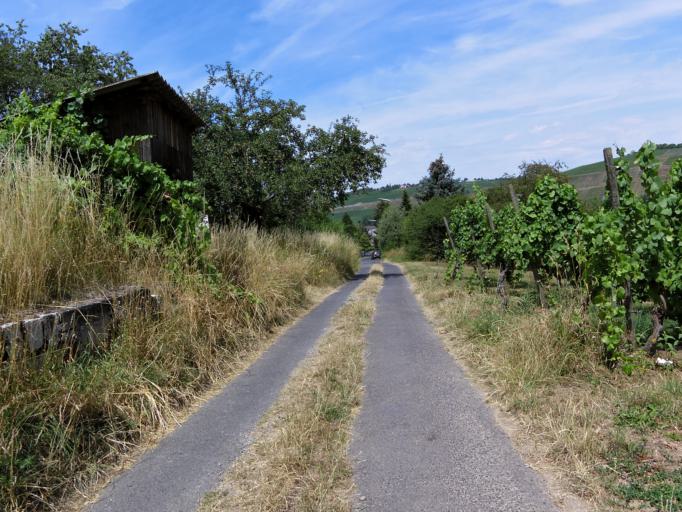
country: DE
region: Bavaria
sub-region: Regierungsbezirk Unterfranken
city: Randersacker
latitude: 49.7571
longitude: 9.9633
